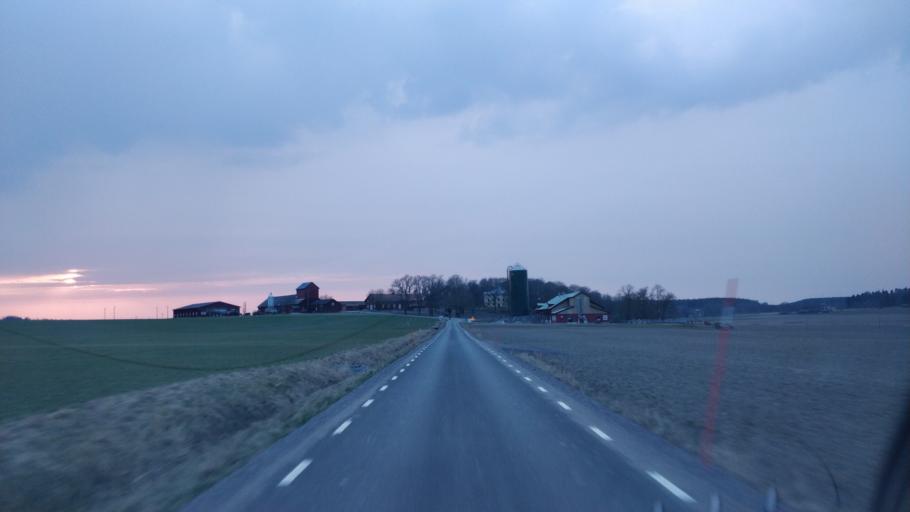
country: SE
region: Uppsala
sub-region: Enkopings Kommun
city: Orsundsbro
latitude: 59.7380
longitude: 17.1869
